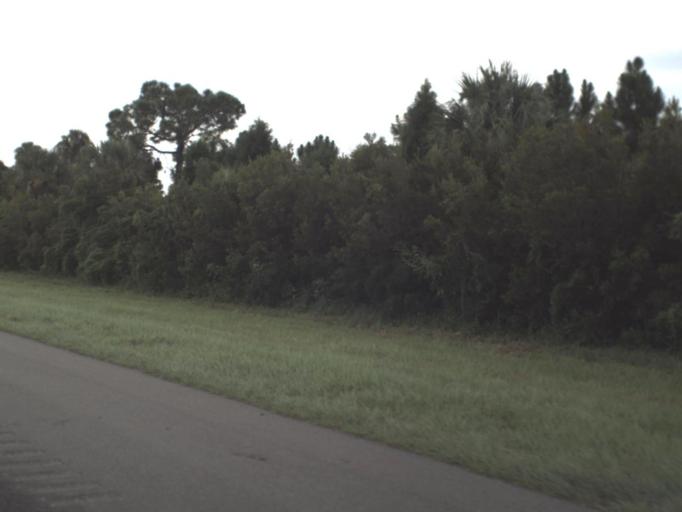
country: US
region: Florida
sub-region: Sarasota County
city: Nokomis
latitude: 27.1278
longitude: -82.4023
